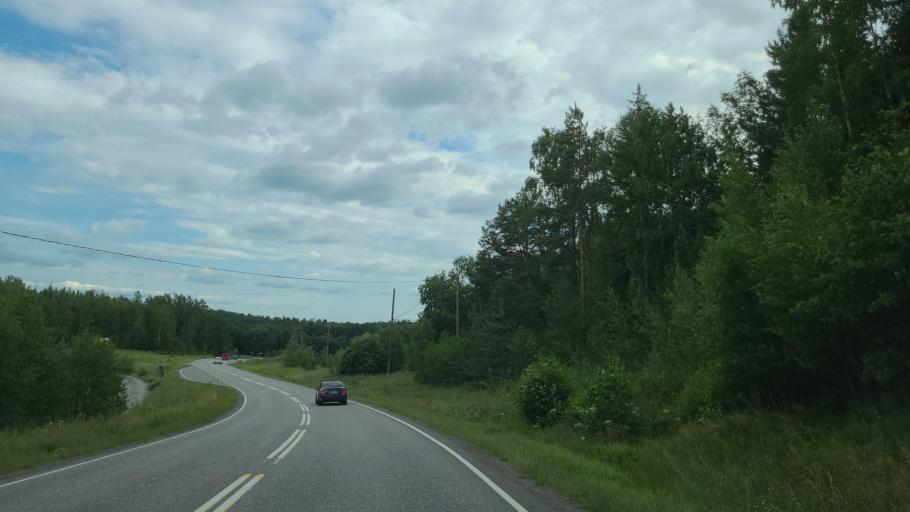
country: FI
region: Varsinais-Suomi
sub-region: Turku
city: Rymaettylae
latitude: 60.3882
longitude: 21.9150
